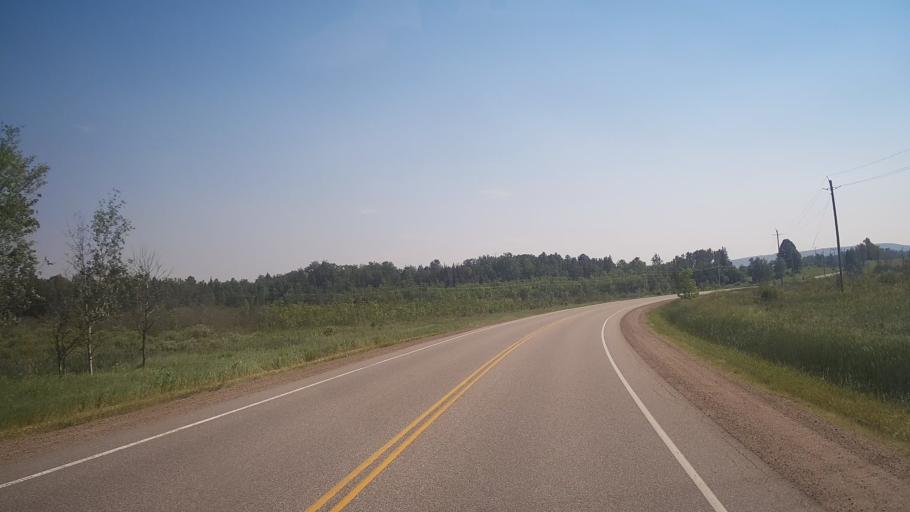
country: CA
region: Ontario
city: Petawawa
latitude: 45.5507
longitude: -77.4266
